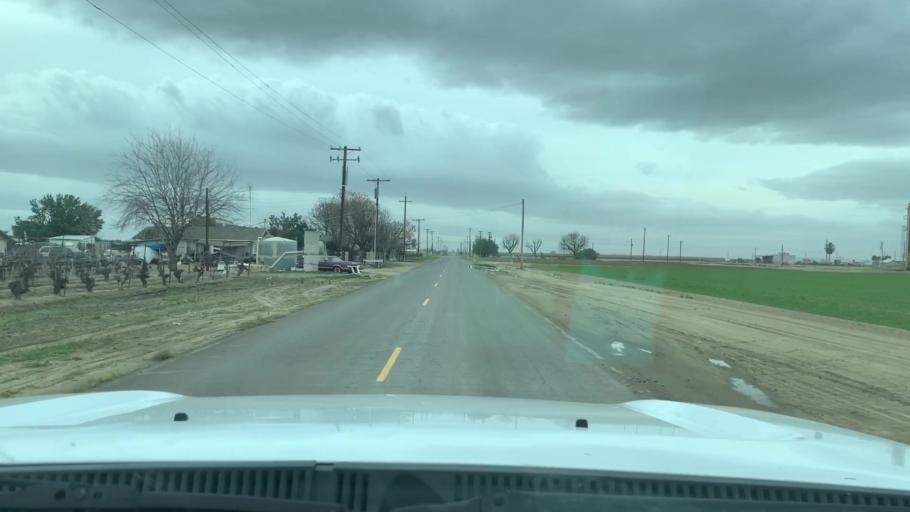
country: US
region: California
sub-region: Kern County
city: Shafter
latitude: 35.5292
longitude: -119.2741
